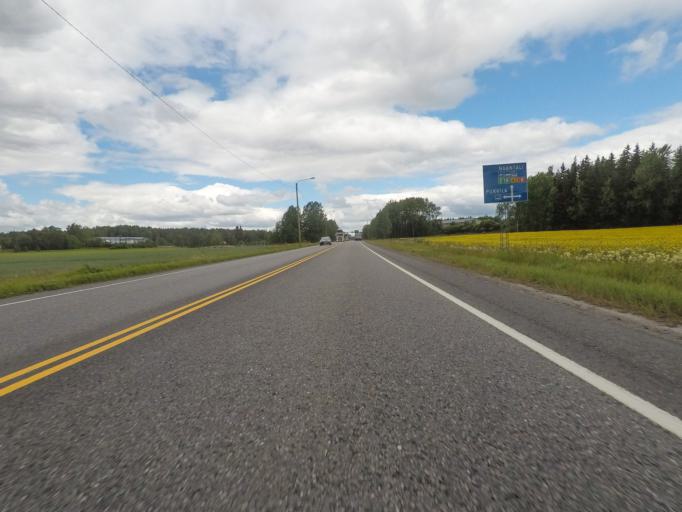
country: FI
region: Varsinais-Suomi
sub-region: Turku
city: Piikkioe
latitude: 60.4488
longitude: 22.4652
